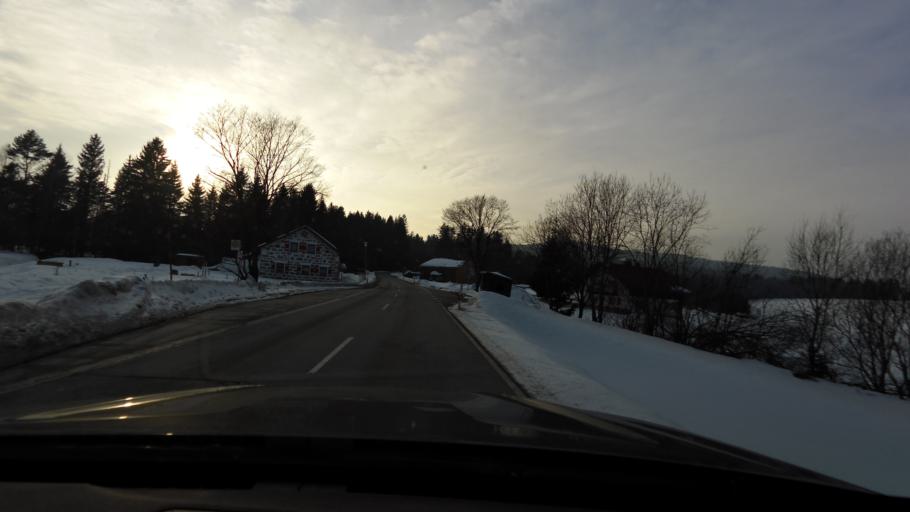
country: DE
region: Bavaria
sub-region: Lower Bavaria
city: Haidmuhle
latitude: 48.8287
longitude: 13.7676
